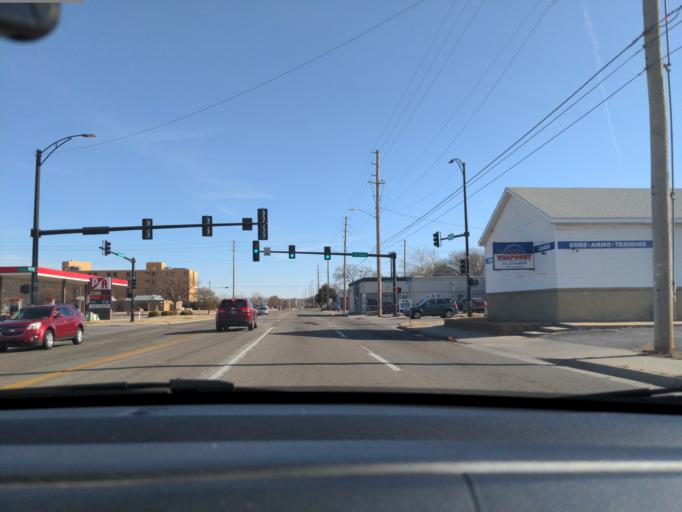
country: US
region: Kansas
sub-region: Sedgwick County
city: Wichita
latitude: 37.6949
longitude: -97.3765
